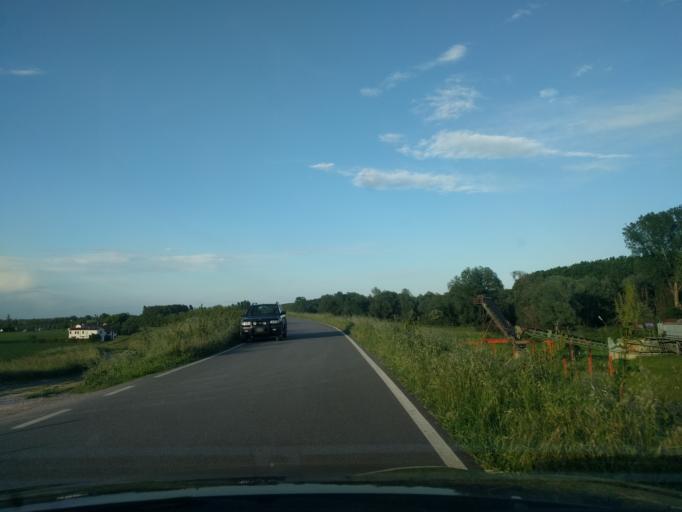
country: IT
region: Emilia-Romagna
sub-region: Provincia di Ferrara
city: Ro
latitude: 44.9650
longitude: 11.7731
